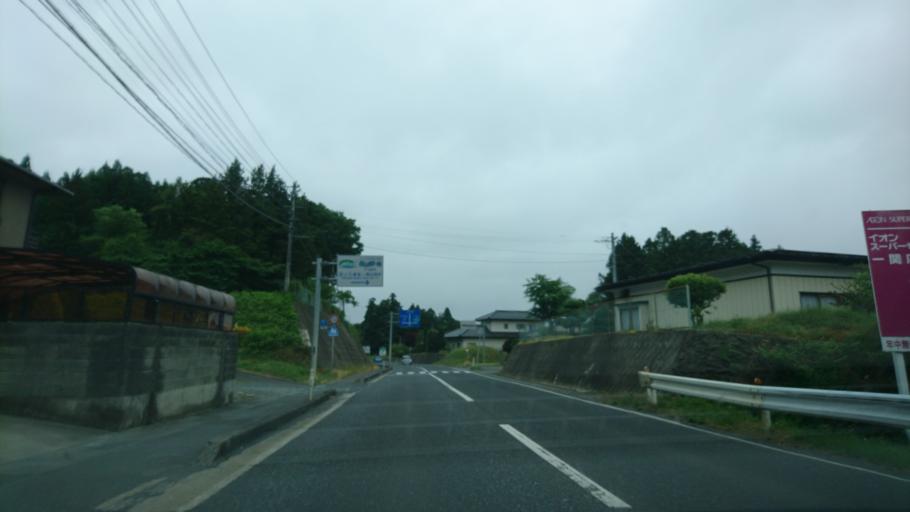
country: JP
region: Iwate
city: Ichinoseki
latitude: 38.9369
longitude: 141.1667
